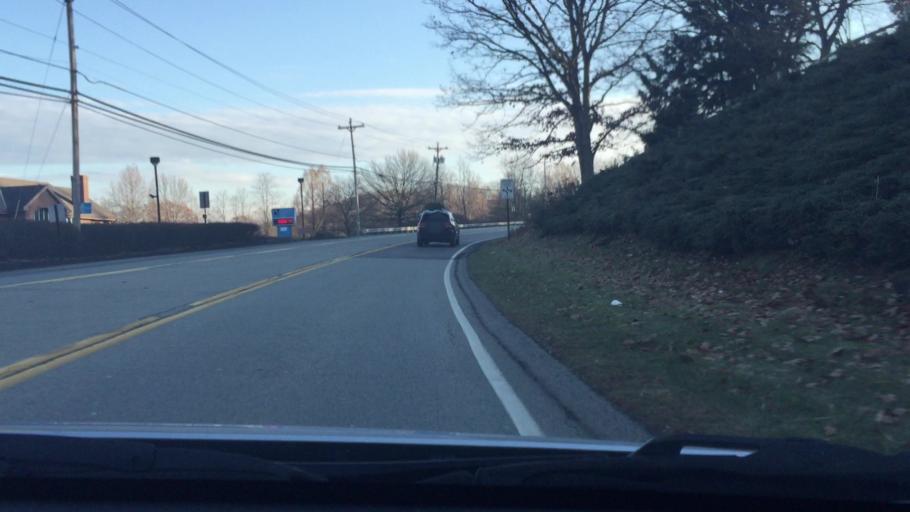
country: US
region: Pennsylvania
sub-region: Allegheny County
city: Bradford Woods
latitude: 40.6135
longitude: -80.0901
